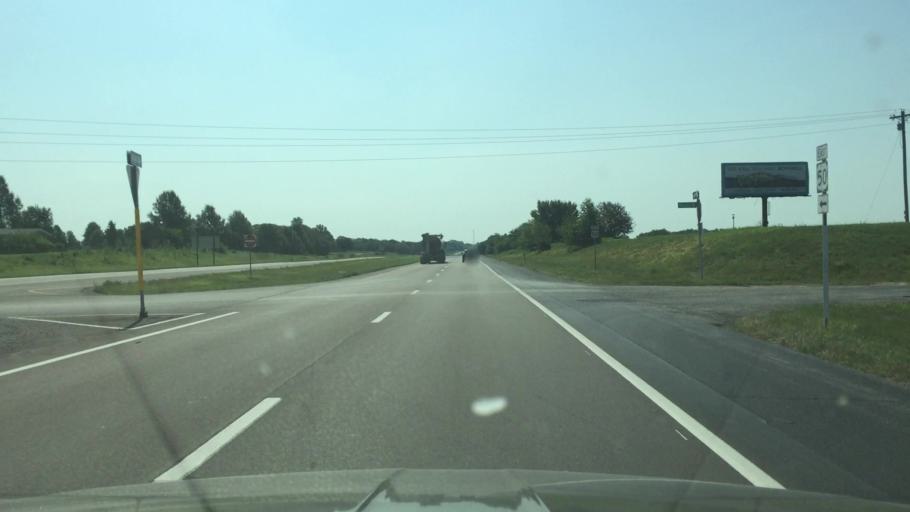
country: US
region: Missouri
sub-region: Pettis County
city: La Monte
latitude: 38.7477
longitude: -93.3413
